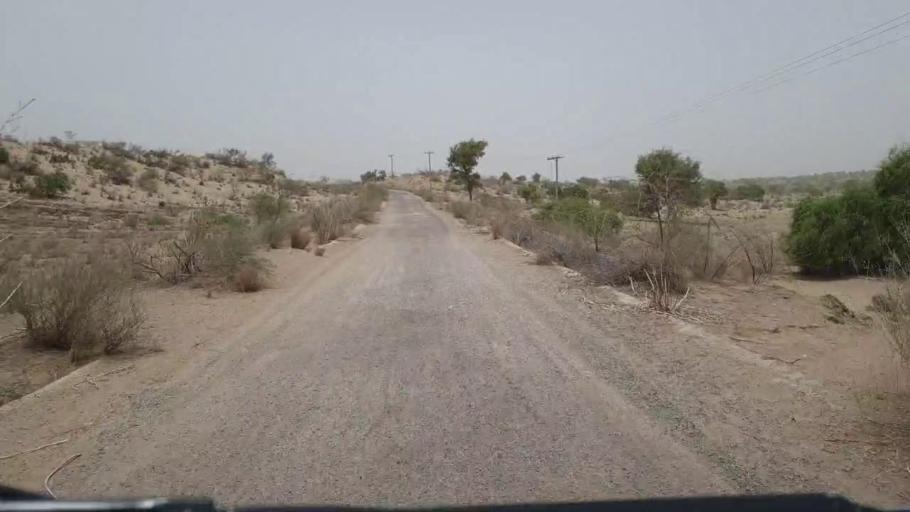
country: PK
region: Sindh
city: Naukot
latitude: 24.7543
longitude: 69.5523
